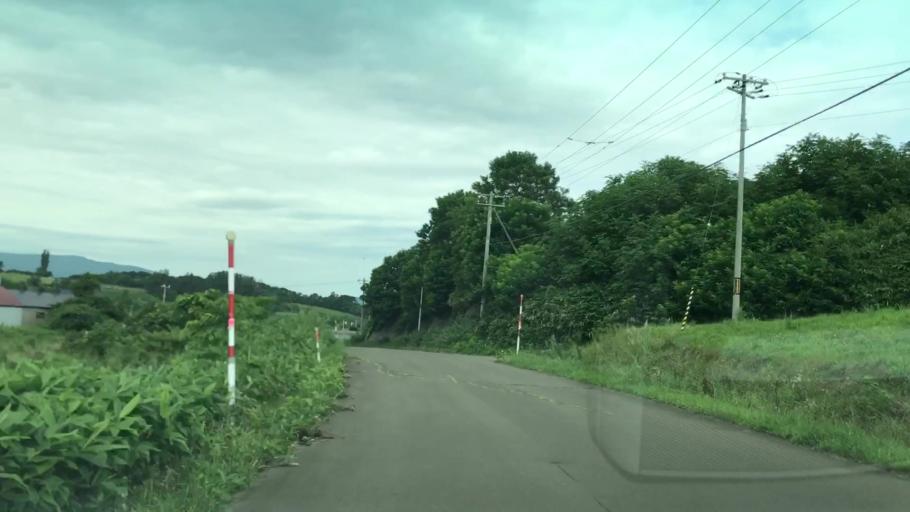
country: JP
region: Hokkaido
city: Yoichi
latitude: 43.1765
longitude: 140.8250
